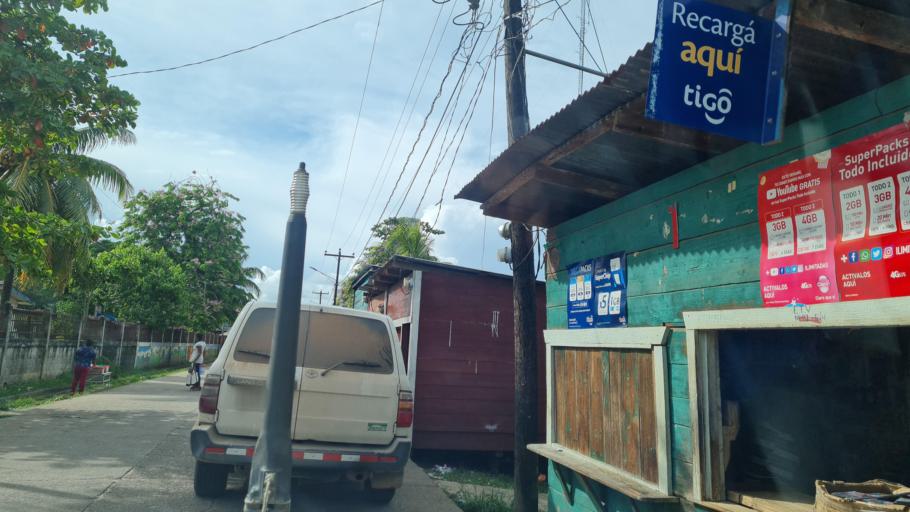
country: NI
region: Atlantico Norte (RAAN)
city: Waspam
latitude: 14.7417
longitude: -83.9712
